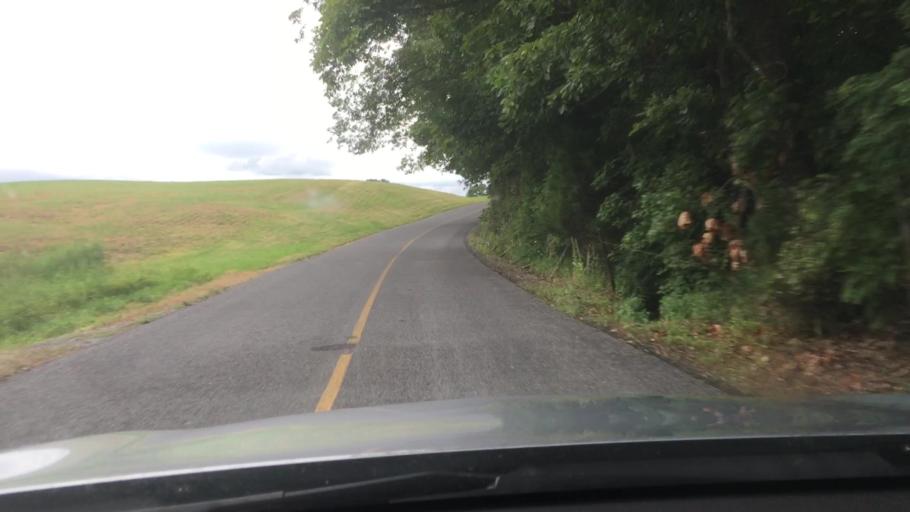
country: US
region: Pennsylvania
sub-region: Franklin County
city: Greencastle
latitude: 39.8701
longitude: -77.7975
